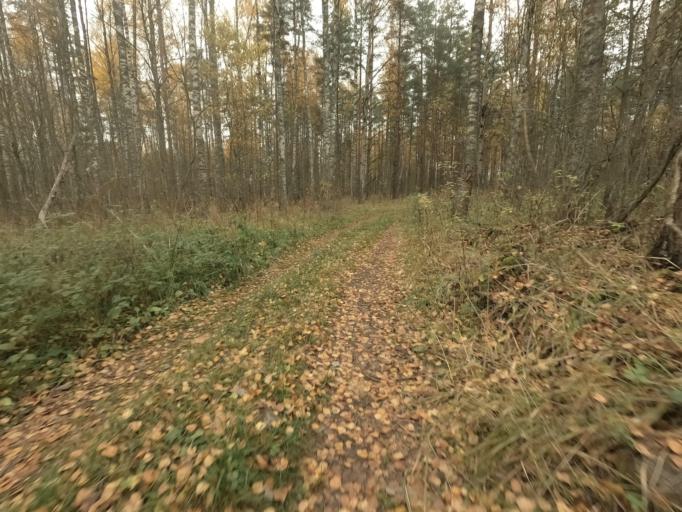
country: RU
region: Leningrad
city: Kirovsk
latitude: 59.8574
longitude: 30.9985
